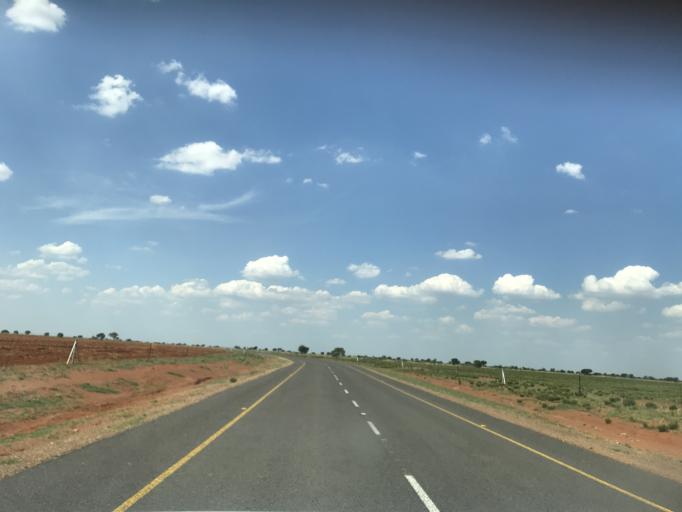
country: BW
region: South East
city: Janeng
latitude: -25.5370
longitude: 25.6168
